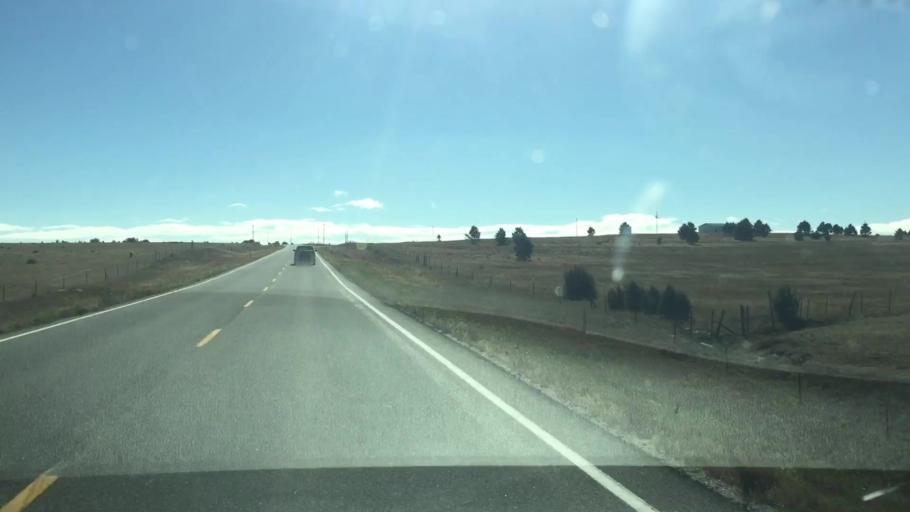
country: US
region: Colorado
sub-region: Elbert County
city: Kiowa
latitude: 39.3347
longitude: -104.4229
